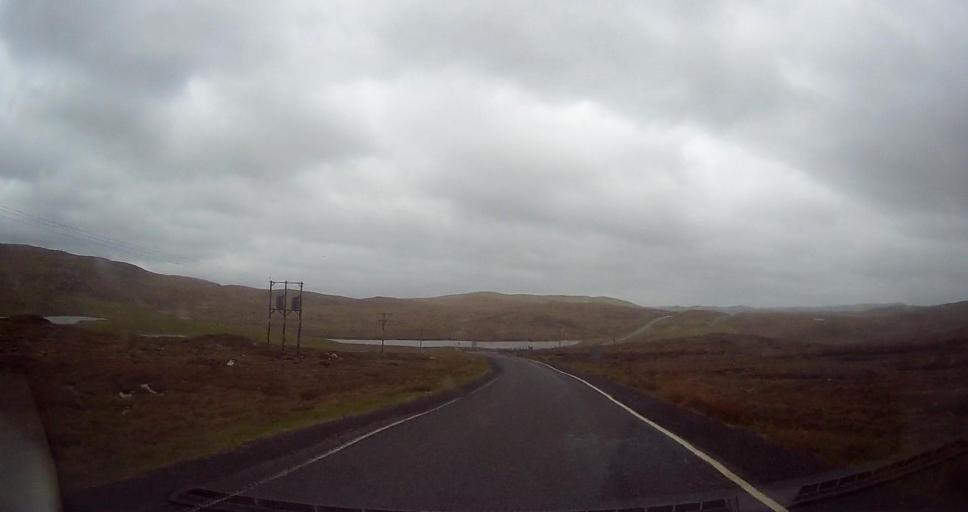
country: GB
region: Scotland
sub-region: Shetland Islands
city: Lerwick
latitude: 60.4796
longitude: -1.4115
